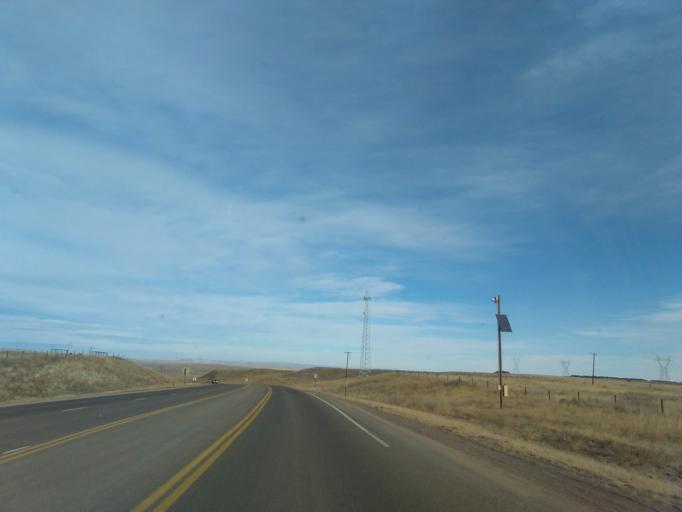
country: US
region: Wyoming
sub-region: Laramie County
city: Pine Bluffs
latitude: 41.4424
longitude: -104.3455
